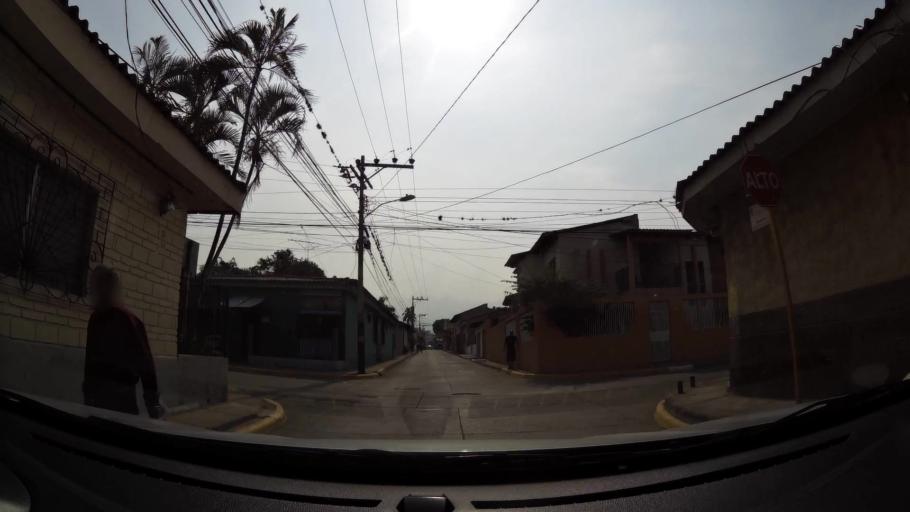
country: HN
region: Comayagua
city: Comayagua
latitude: 14.4609
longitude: -87.6440
